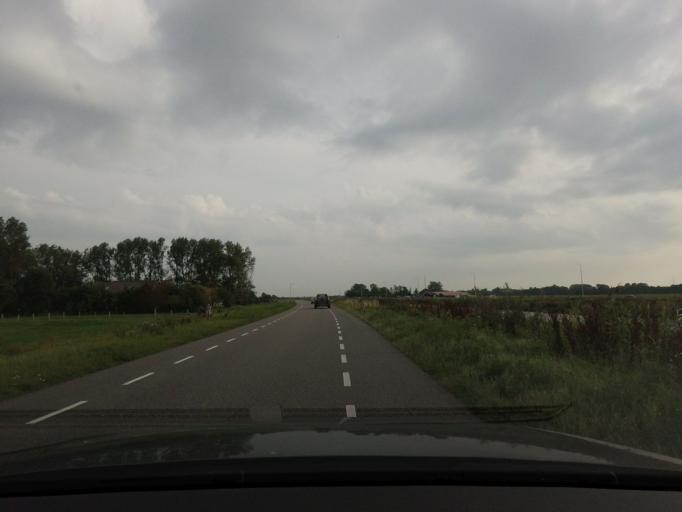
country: NL
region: North Holland
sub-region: Gemeente Schagen
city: Harenkarspel
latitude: 52.7007
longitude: 4.7191
